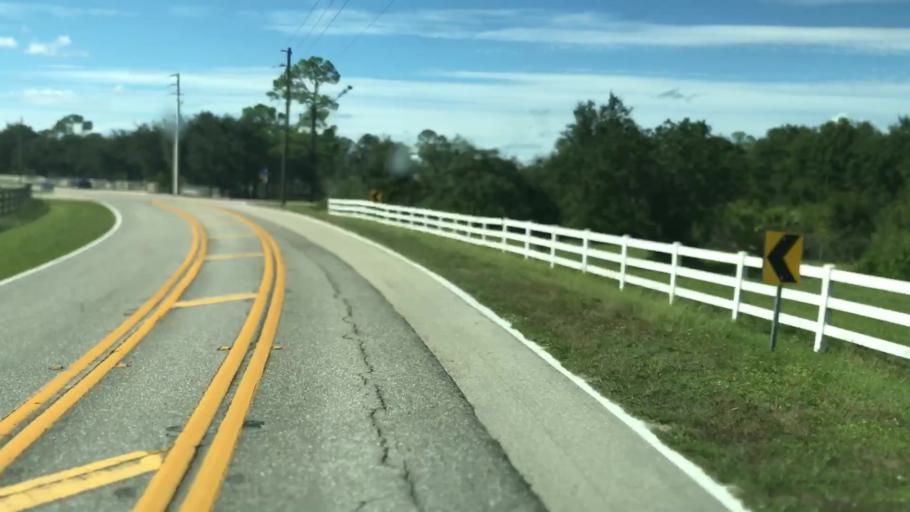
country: US
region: Florida
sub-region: Lee County
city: Olga
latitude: 26.7283
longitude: -81.6836
